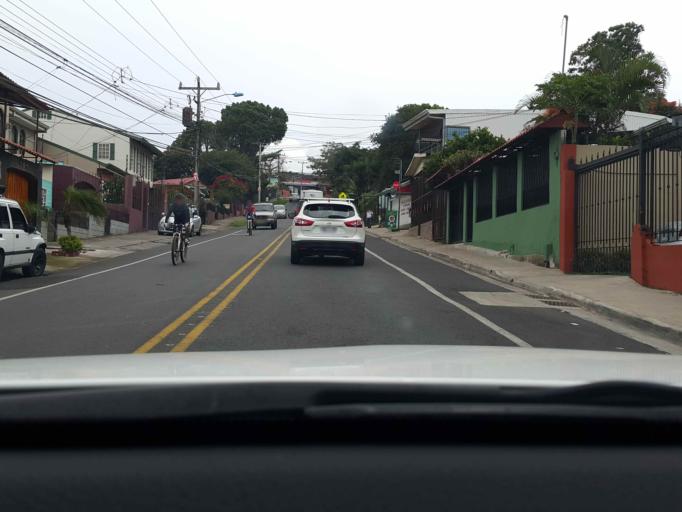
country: CR
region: Heredia
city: San Josecito
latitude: 10.0175
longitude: -84.0990
